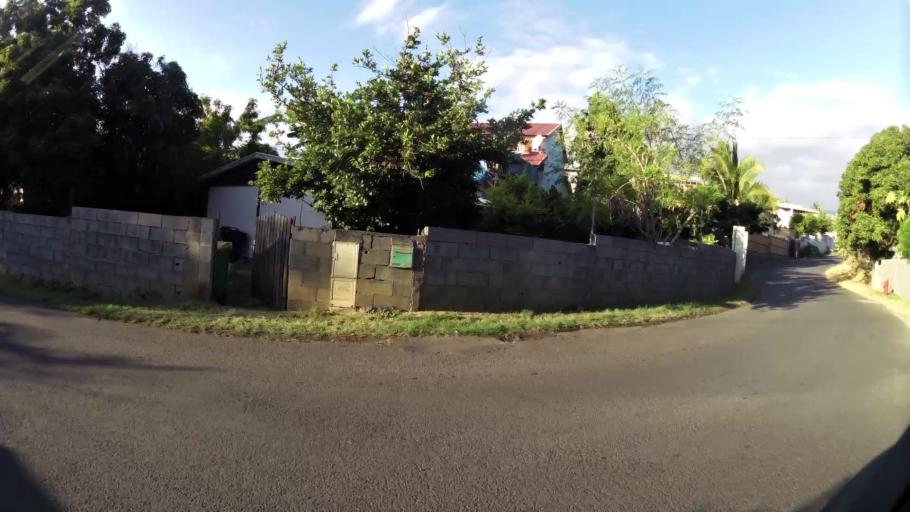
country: RE
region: Reunion
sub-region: Reunion
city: Trois-Bassins
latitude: -21.0947
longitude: 55.2403
